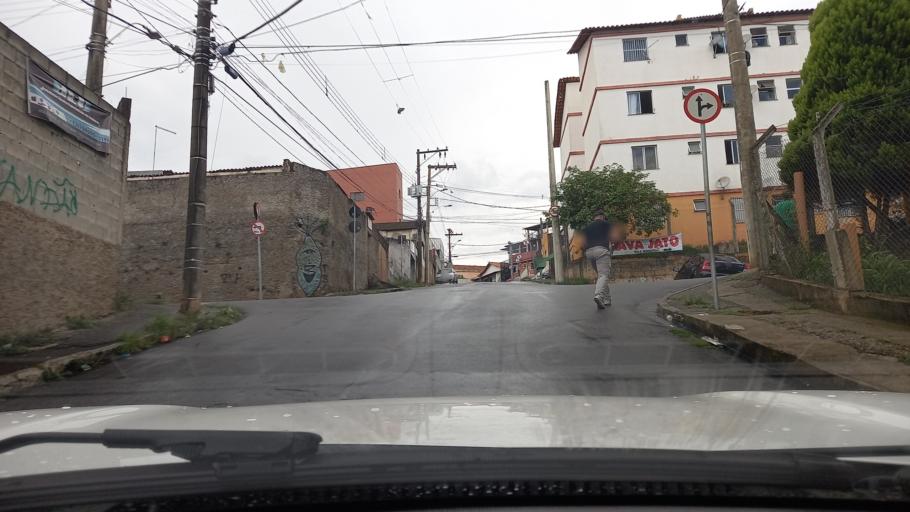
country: BR
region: Minas Gerais
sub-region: Belo Horizonte
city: Belo Horizonte
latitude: -19.9014
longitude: -43.9514
